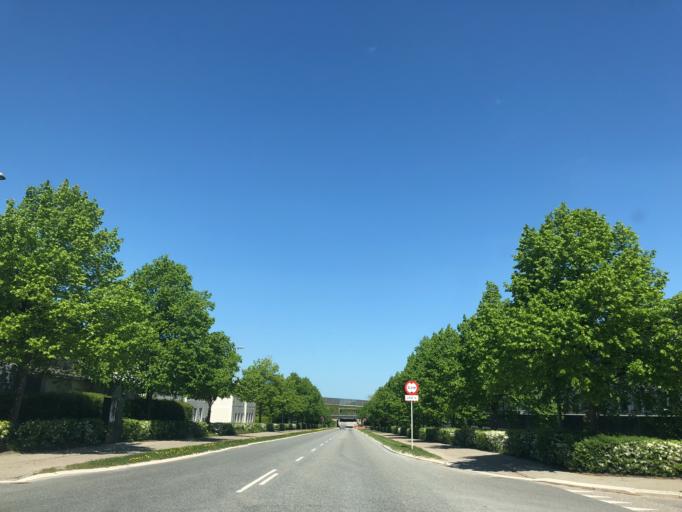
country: DK
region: Zealand
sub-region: Roskilde Kommune
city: Vindinge
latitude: 55.6458
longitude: 12.1442
